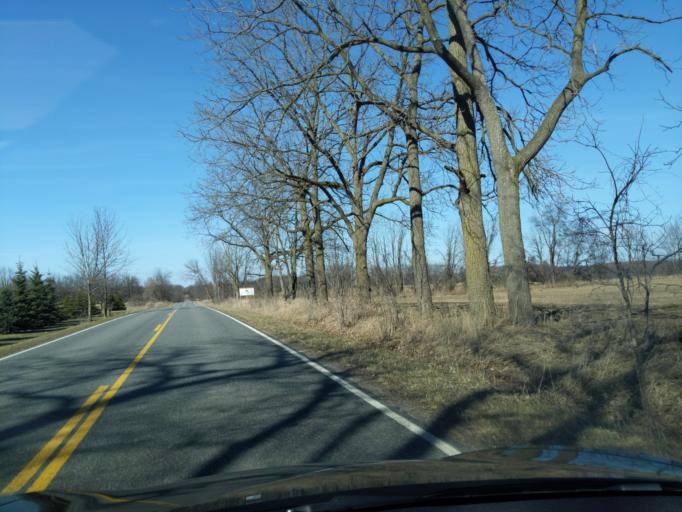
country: US
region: Michigan
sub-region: Ionia County
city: Saranac
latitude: 42.9252
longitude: -85.1341
